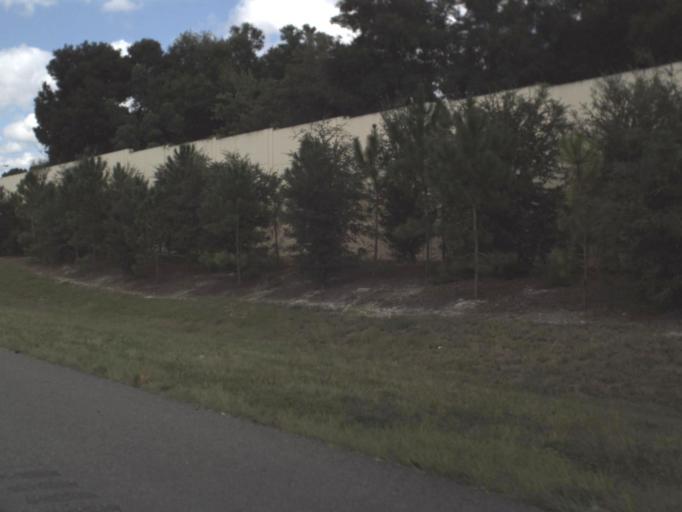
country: US
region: Florida
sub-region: Orange County
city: Gotha
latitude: 28.5263
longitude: -81.5147
